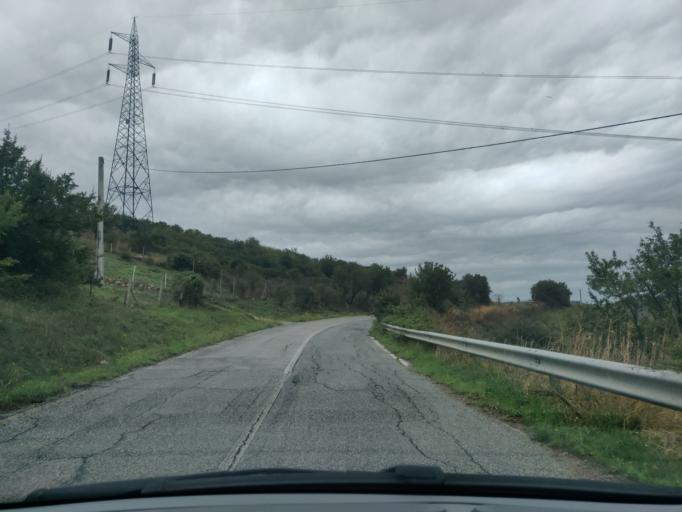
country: IT
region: Latium
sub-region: Citta metropolitana di Roma Capitale
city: Aurelia
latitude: 42.1323
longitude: 11.8411
